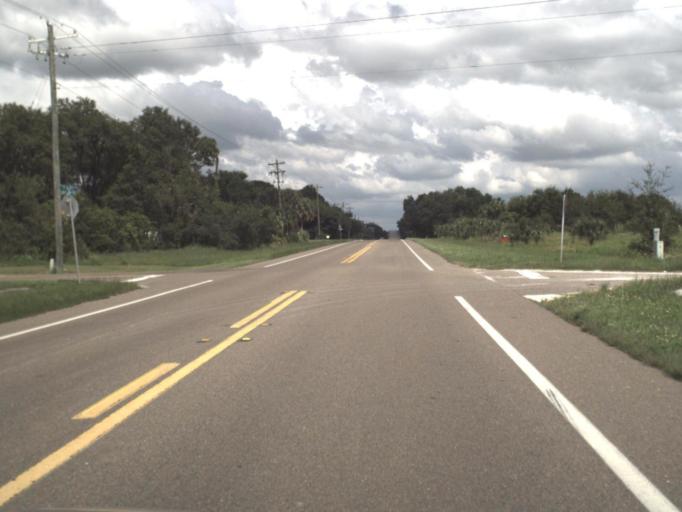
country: US
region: Florida
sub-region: Hardee County
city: Zolfo Springs
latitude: 27.4929
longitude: -81.8340
